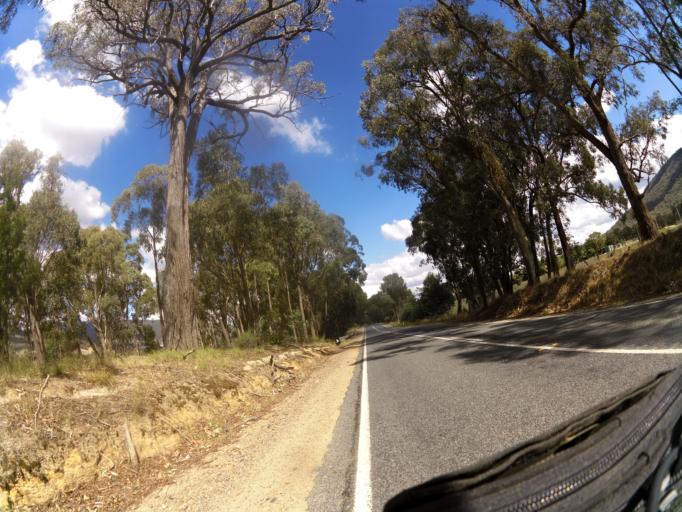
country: AU
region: Victoria
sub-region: Mansfield
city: Mansfield
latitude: -36.8155
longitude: 146.0073
